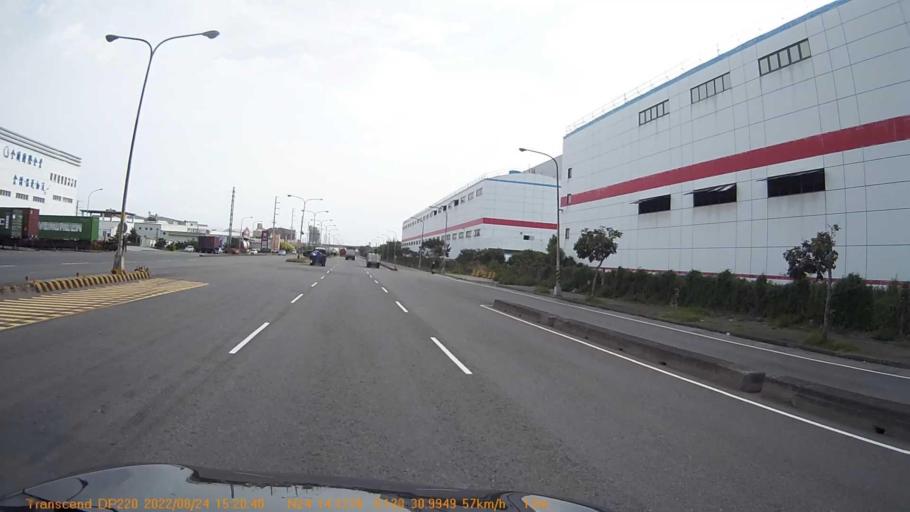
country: TW
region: Taiwan
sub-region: Changhua
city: Chang-hua
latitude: 24.2350
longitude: 120.5164
